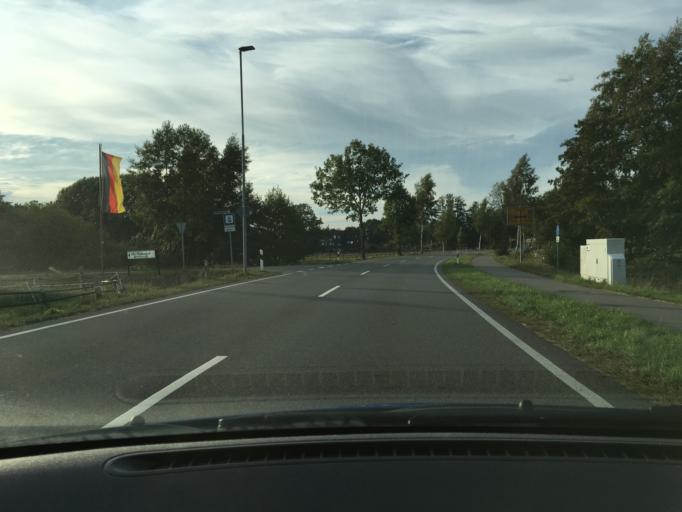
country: DE
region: Lower Saxony
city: Soltau
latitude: 52.9898
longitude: 9.9113
